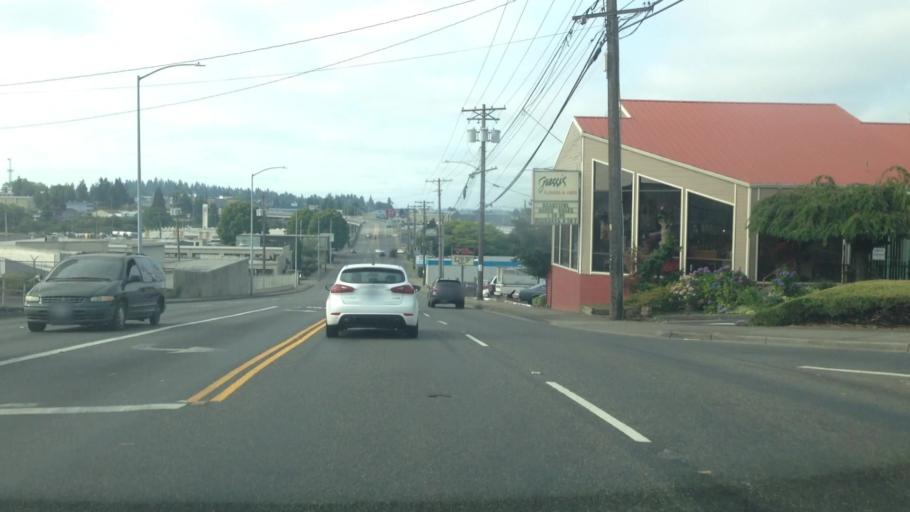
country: US
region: Washington
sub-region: Pierce County
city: Fircrest
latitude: 47.2312
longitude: -122.4837
